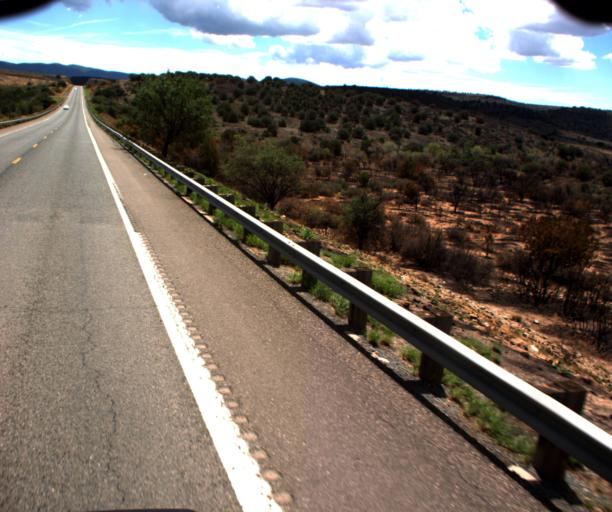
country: US
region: Arizona
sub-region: Yavapai County
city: Camp Verde
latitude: 34.5203
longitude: -112.0364
